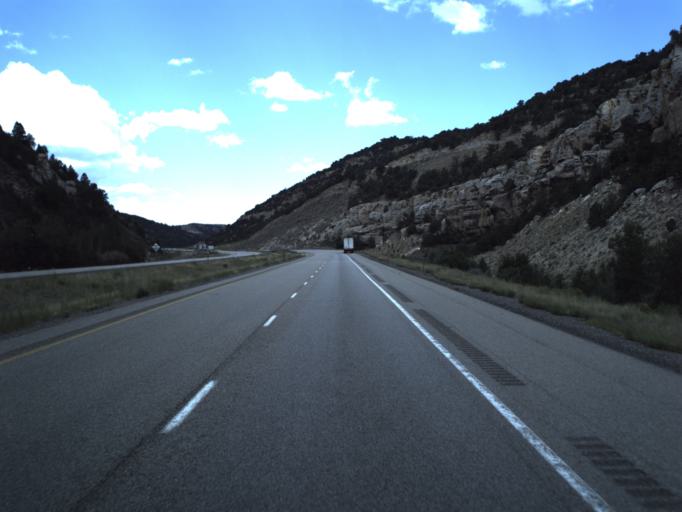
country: US
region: Utah
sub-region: Wayne County
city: Loa
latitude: 38.7578
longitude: -111.4473
